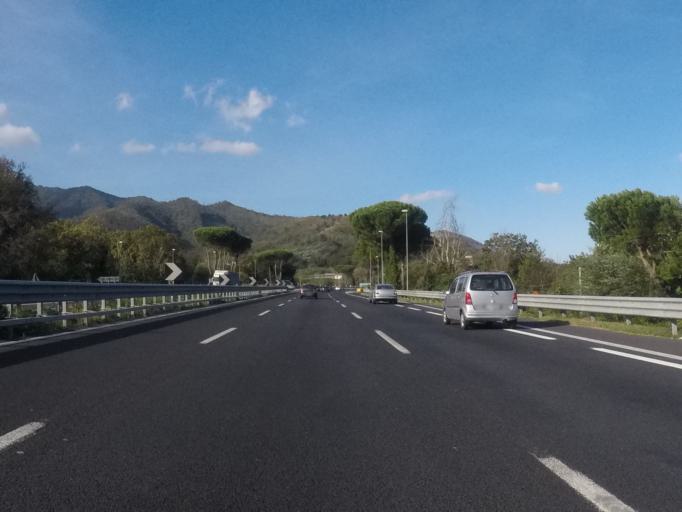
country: IT
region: Campania
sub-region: Provincia di Salerno
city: Mercato San Severino
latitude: 40.7720
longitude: 14.7525
